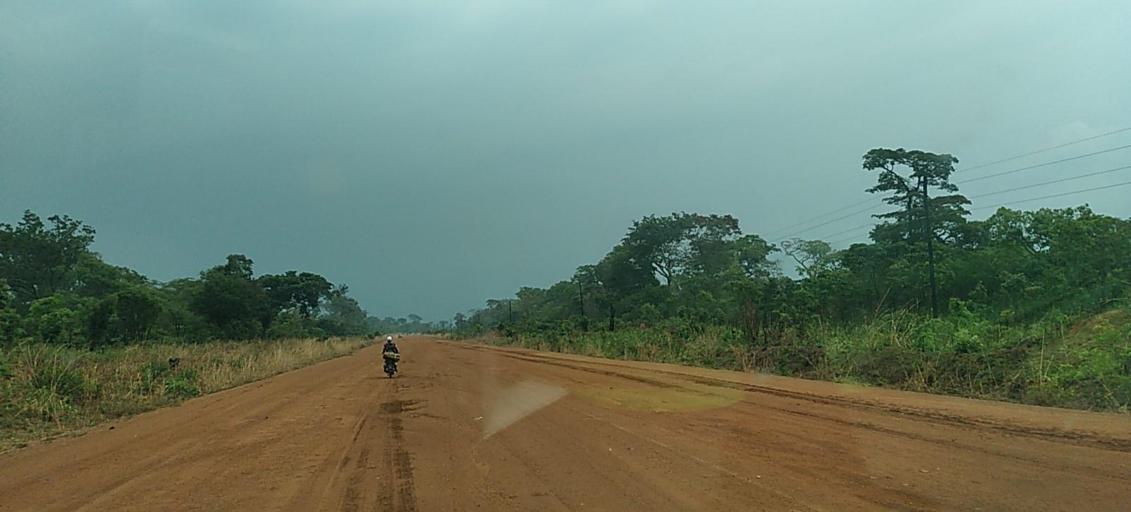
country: ZM
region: North-Western
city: Mwinilunga
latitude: -11.6265
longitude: 24.4023
